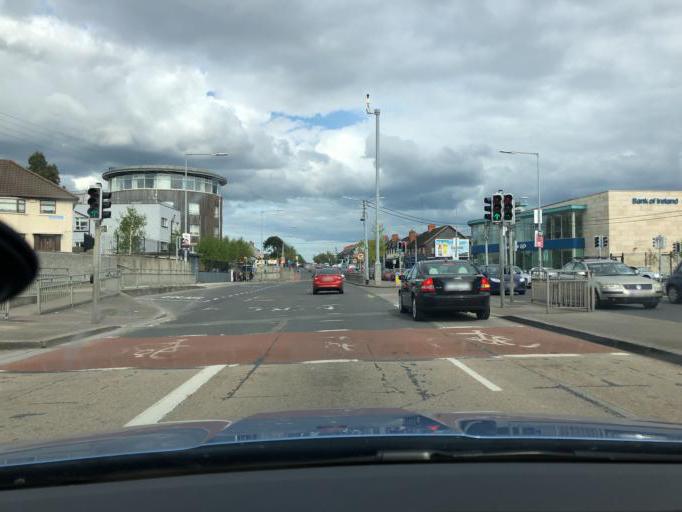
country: IE
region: Leinster
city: Crumlin
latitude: 53.3241
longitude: -6.3291
